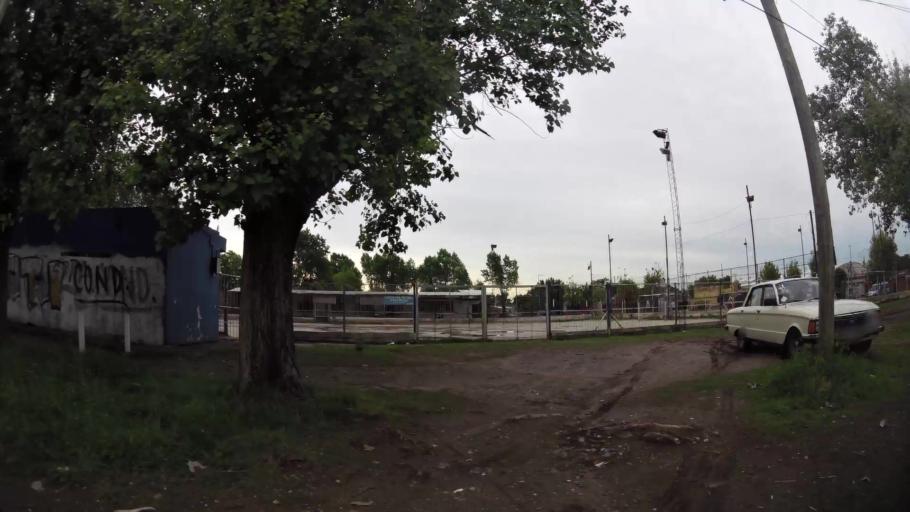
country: AR
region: Buenos Aires
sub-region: Partido de Lanus
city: Lanus
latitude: -34.7250
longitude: -58.3553
